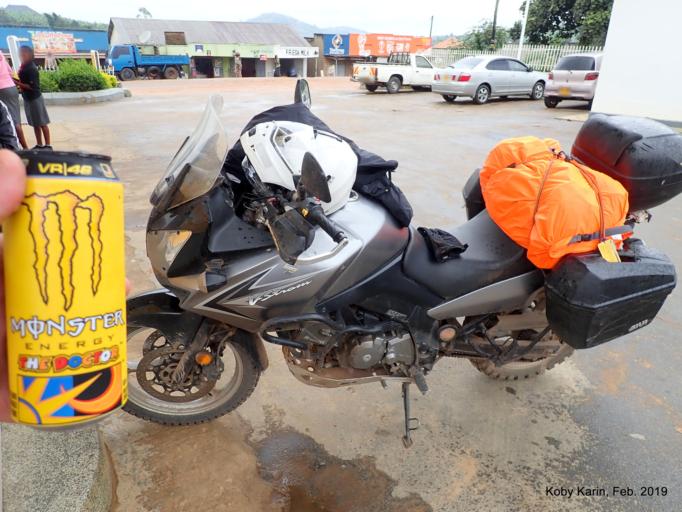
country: UG
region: Western Region
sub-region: Bushenyi District
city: Bushenyi
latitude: -0.5391
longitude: 30.1268
